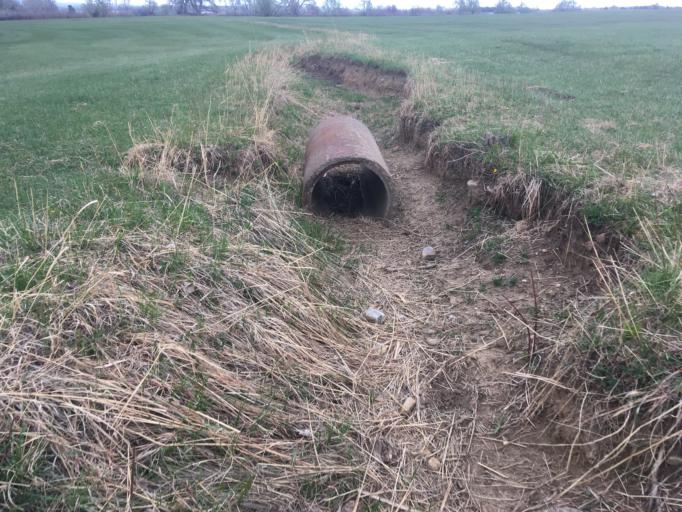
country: US
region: Colorado
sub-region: Boulder County
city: Superior
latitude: 39.9682
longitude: -105.2117
